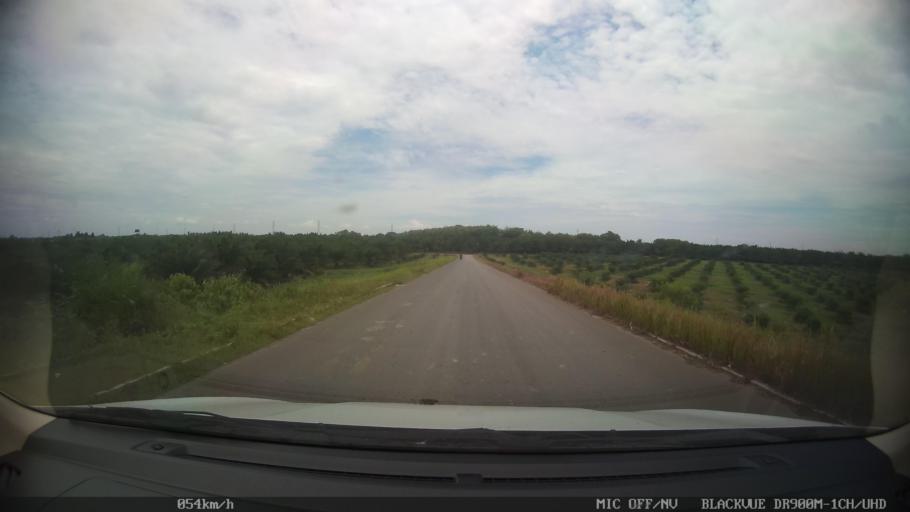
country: ID
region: North Sumatra
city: Sunggal
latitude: 3.6346
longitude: 98.5813
